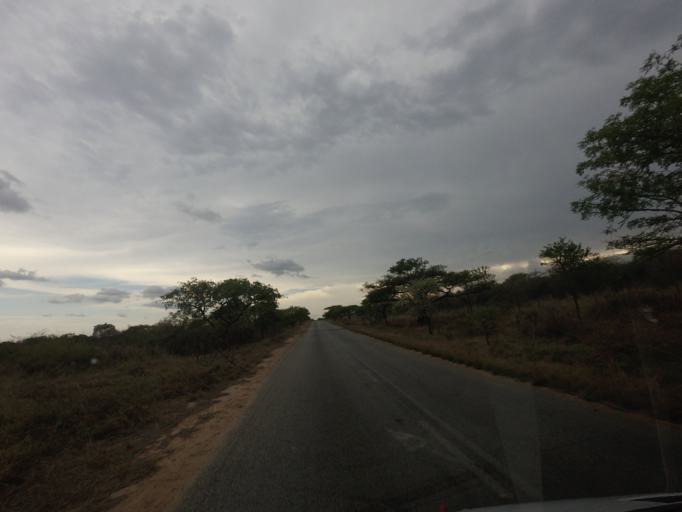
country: ZA
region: Limpopo
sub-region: Mopani District Municipality
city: Hoedspruit
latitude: -24.5179
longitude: 30.9602
